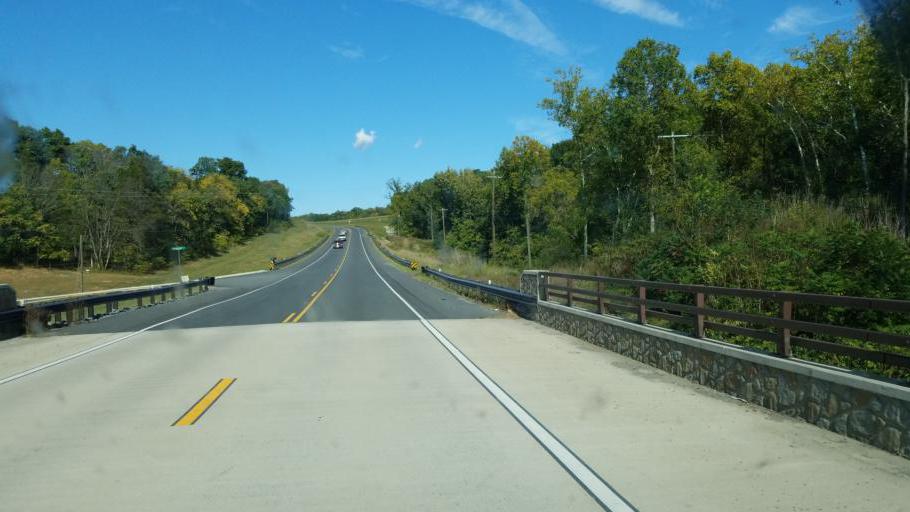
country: US
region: Virginia
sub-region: Warren County
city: Front Royal
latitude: 38.8692
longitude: -78.2499
